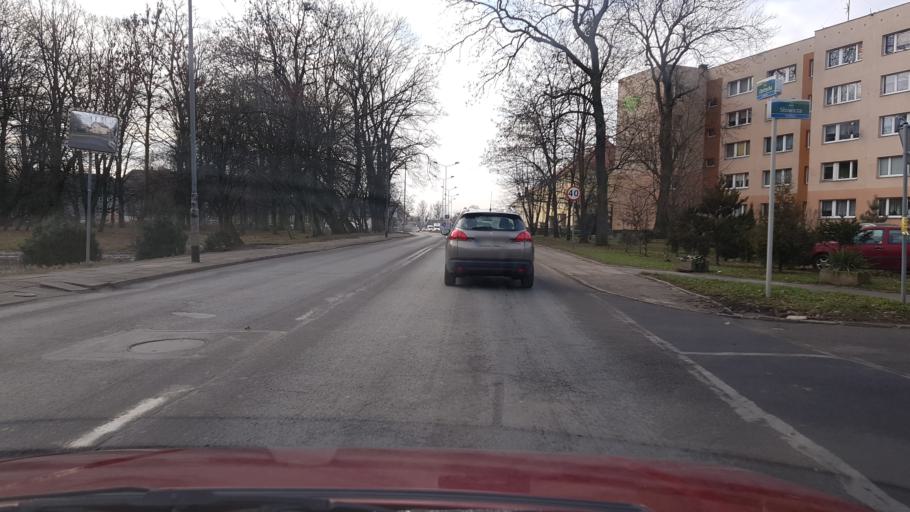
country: PL
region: West Pomeranian Voivodeship
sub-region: Szczecin
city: Szczecin
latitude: 53.4555
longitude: 14.5668
